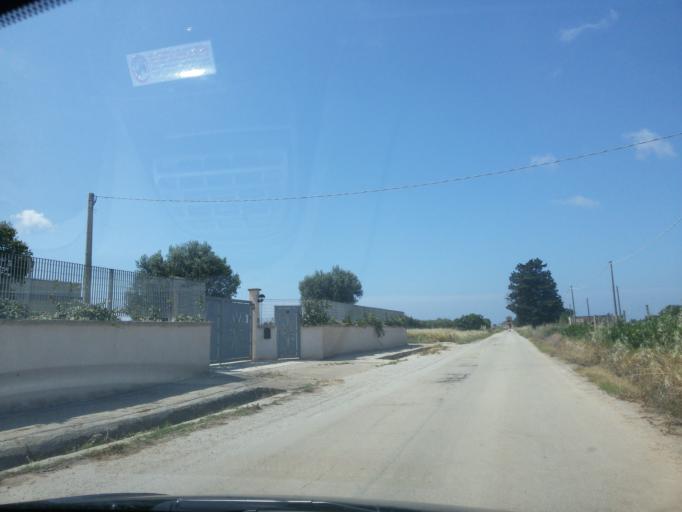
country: IT
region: Apulia
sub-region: Provincia di Brindisi
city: Brindisi
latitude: 40.6566
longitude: 17.8524
